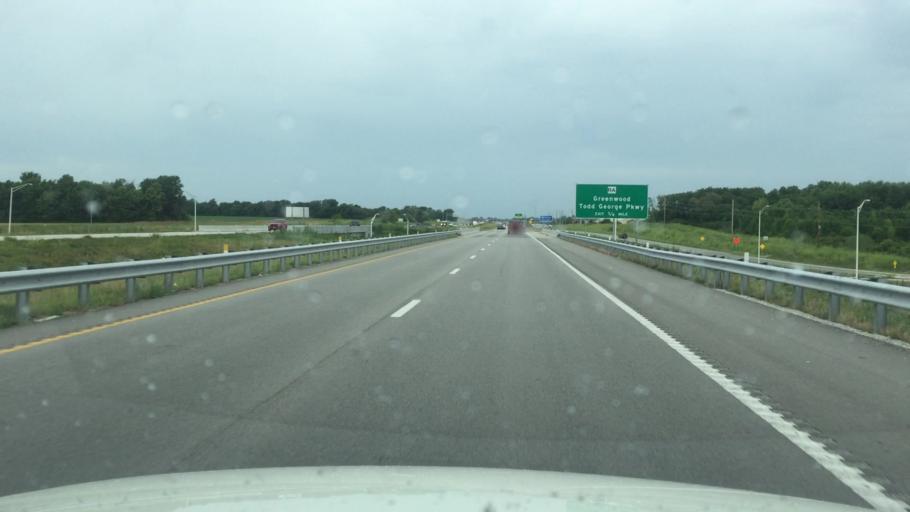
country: US
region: Missouri
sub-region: Jackson County
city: Greenwood
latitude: 38.9017
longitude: -94.3171
